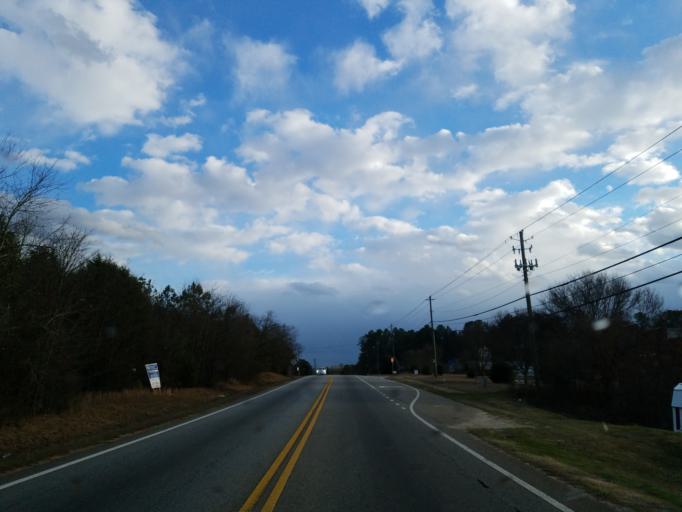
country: US
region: Georgia
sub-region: Henry County
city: Stockbridge
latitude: 33.5297
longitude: -84.1978
